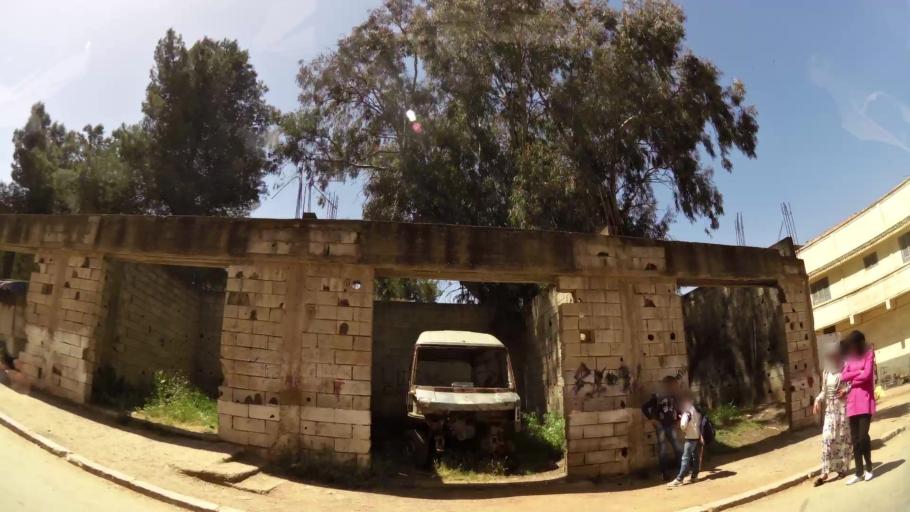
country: MA
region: Rabat-Sale-Zemmour-Zaer
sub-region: Khemisset
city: Khemisset
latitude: 33.8111
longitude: -6.0737
